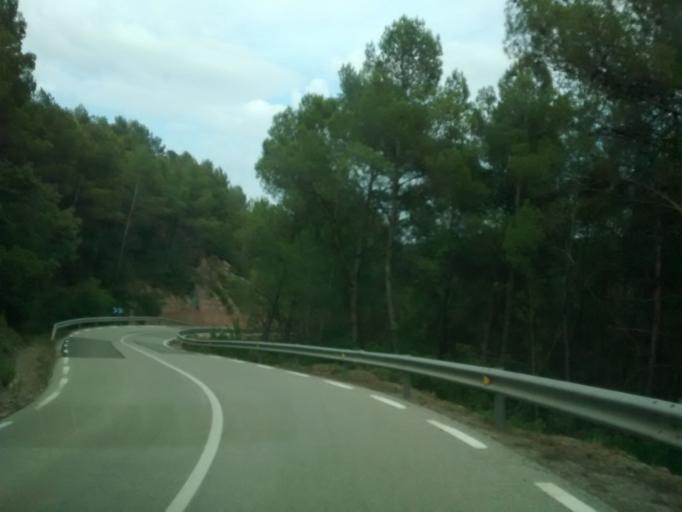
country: ES
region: Catalonia
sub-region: Provincia de Barcelona
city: Rajadell
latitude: 41.7626
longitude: 1.7126
